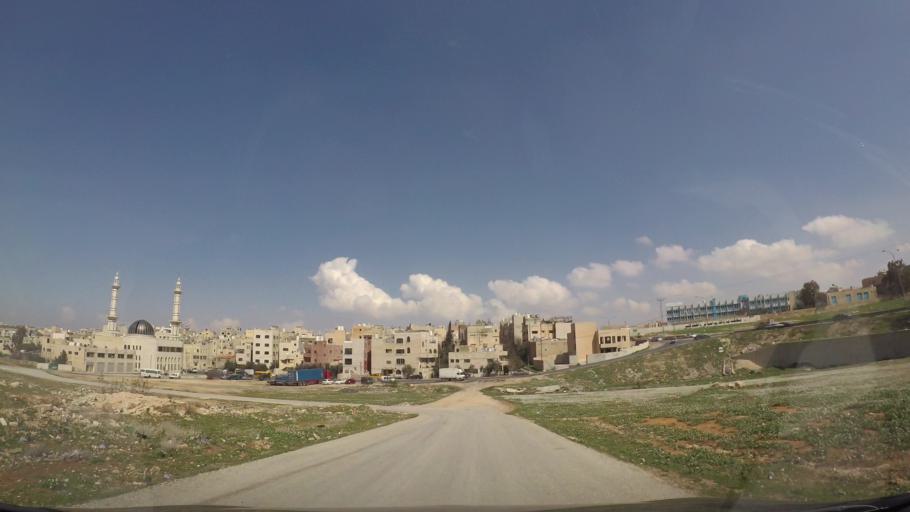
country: JO
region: Zarqa
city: Russeifa
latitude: 31.9853
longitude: 36.0172
